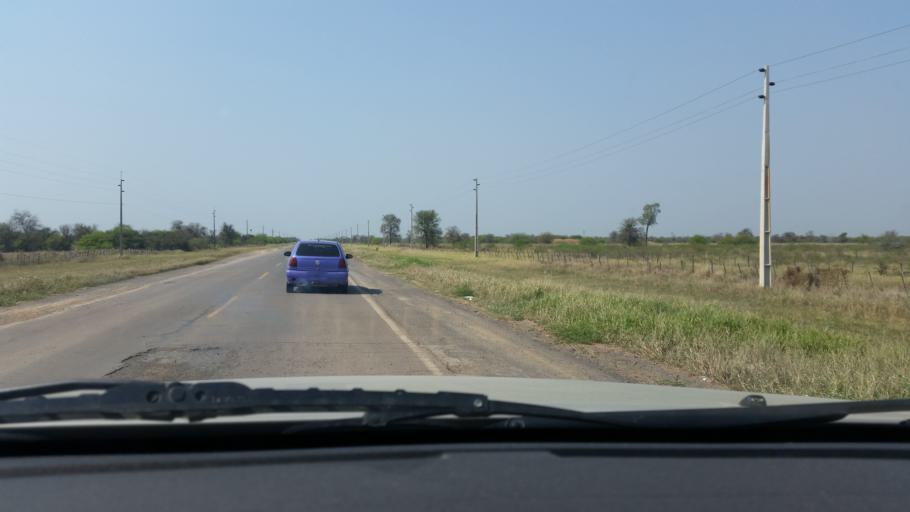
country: PY
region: Boqueron
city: Filadelfia
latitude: -22.4399
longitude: -60.0209
